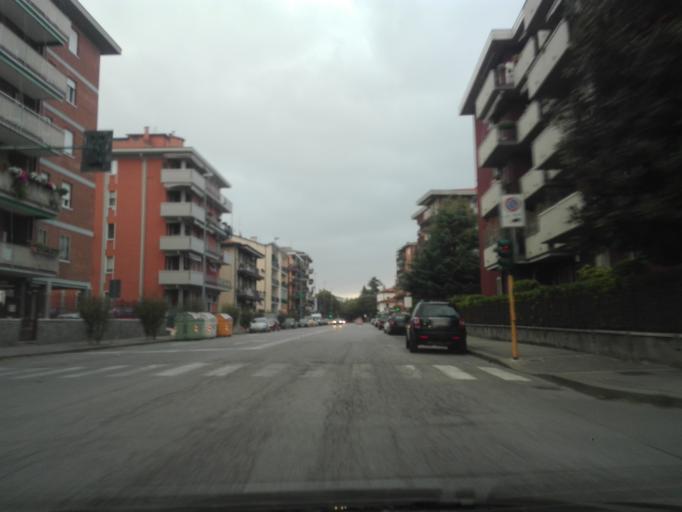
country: IT
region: Veneto
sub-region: Provincia di Verona
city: Verona
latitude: 45.4199
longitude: 10.9632
